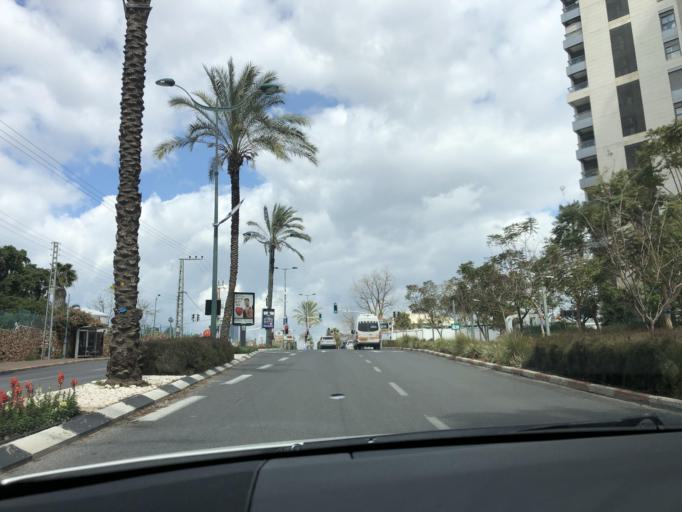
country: IL
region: Central District
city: Hod HaSharon
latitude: 32.1619
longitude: 34.8942
